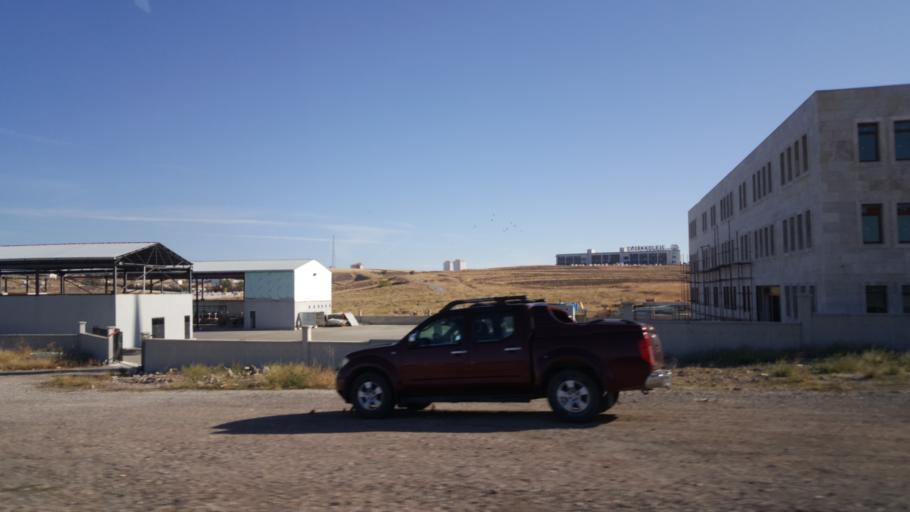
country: TR
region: Ankara
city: Mamak
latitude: 40.0316
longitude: 32.8635
